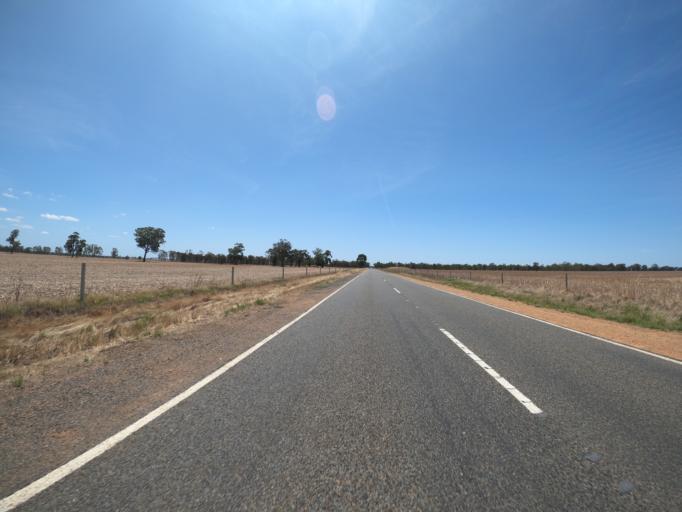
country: AU
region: Victoria
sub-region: Moira
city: Yarrawonga
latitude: -36.1668
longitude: 145.9672
